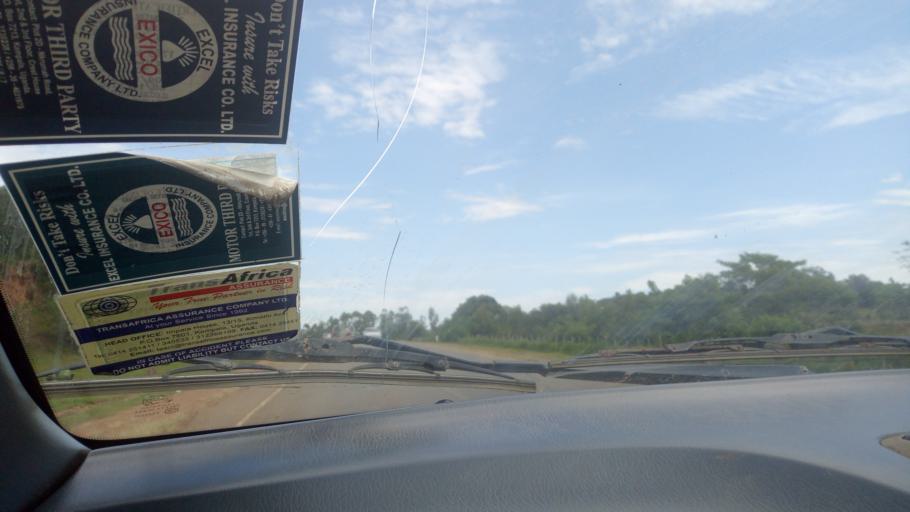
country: UG
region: Western Region
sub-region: Mbarara District
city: Bwizibwera
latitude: -0.3535
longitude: 30.5689
